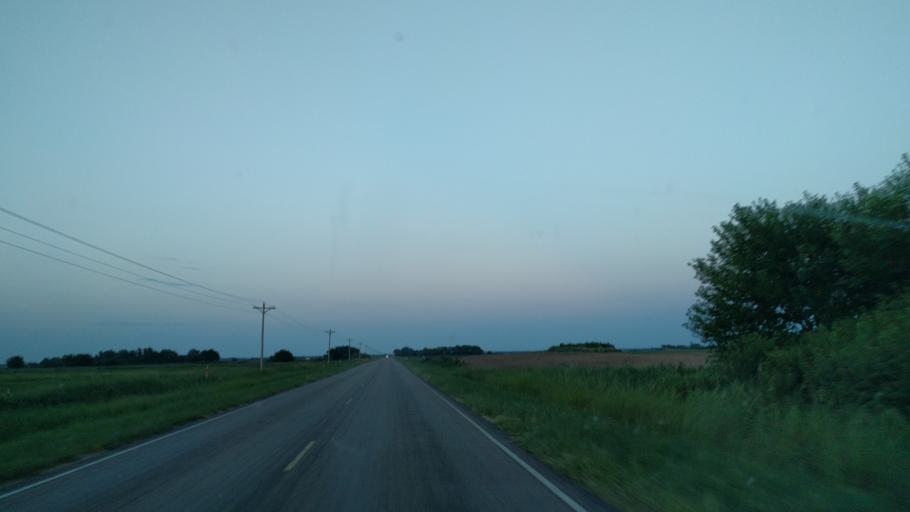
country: US
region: Kansas
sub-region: Reno County
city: Nickerson
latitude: 38.2177
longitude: -98.1204
